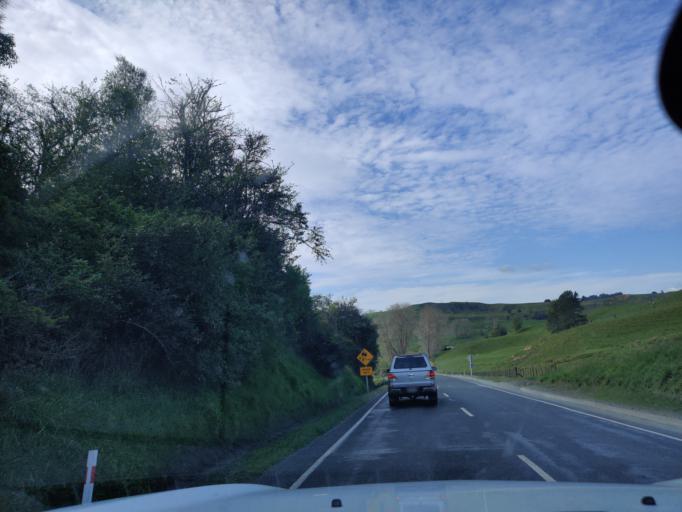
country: NZ
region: Waikato
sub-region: Otorohanga District
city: Otorohanga
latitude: -38.3823
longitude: 175.1308
